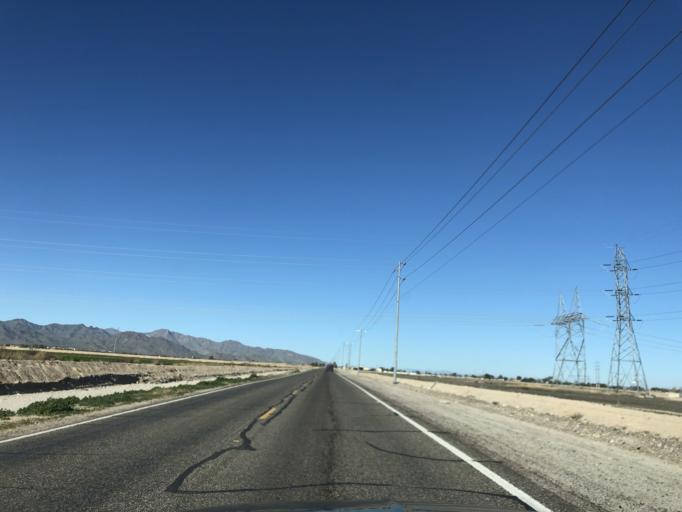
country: US
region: Arizona
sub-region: Maricopa County
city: Buckeye
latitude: 33.4107
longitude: -112.5042
